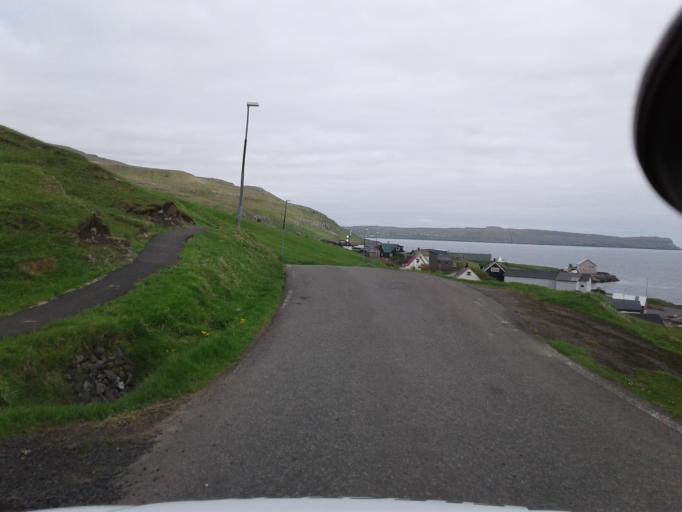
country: FO
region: Streymoy
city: Hoyvik
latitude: 62.0577
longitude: -6.8384
